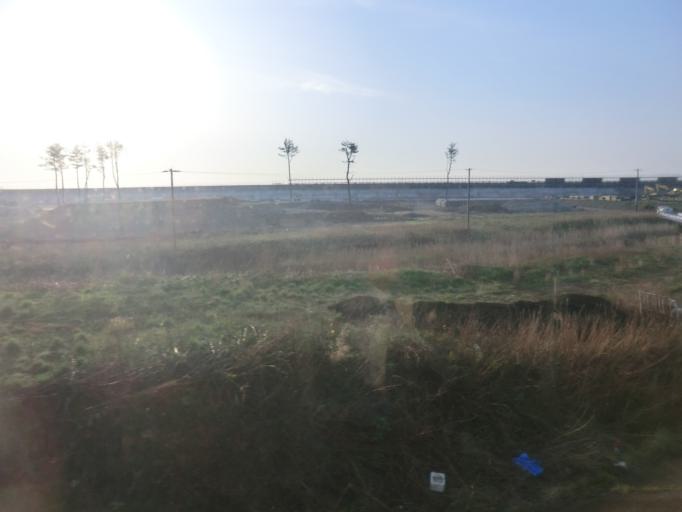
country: JP
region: Iwate
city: Miyako
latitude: 40.1104
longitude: 141.8240
